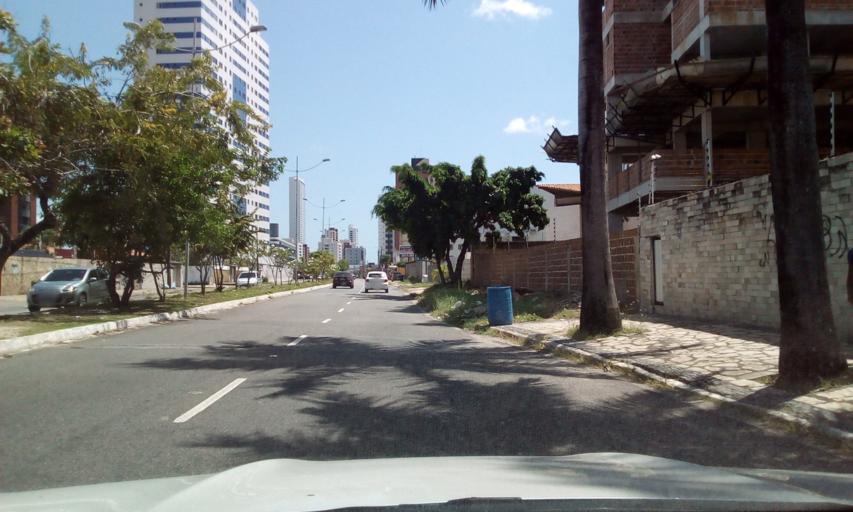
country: BR
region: Paraiba
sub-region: Joao Pessoa
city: Joao Pessoa
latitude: -7.0922
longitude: -34.8379
